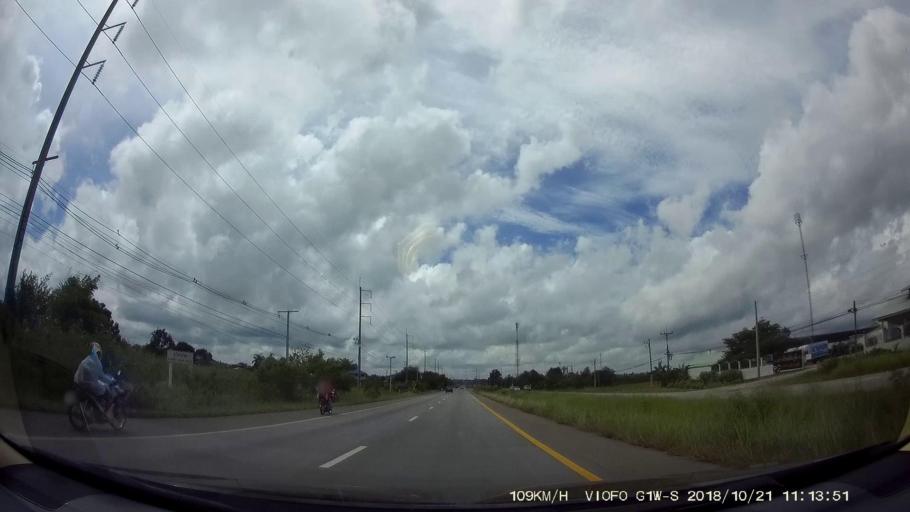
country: TH
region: Chaiyaphum
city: Chaiyaphum
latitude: 15.9112
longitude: 102.1285
